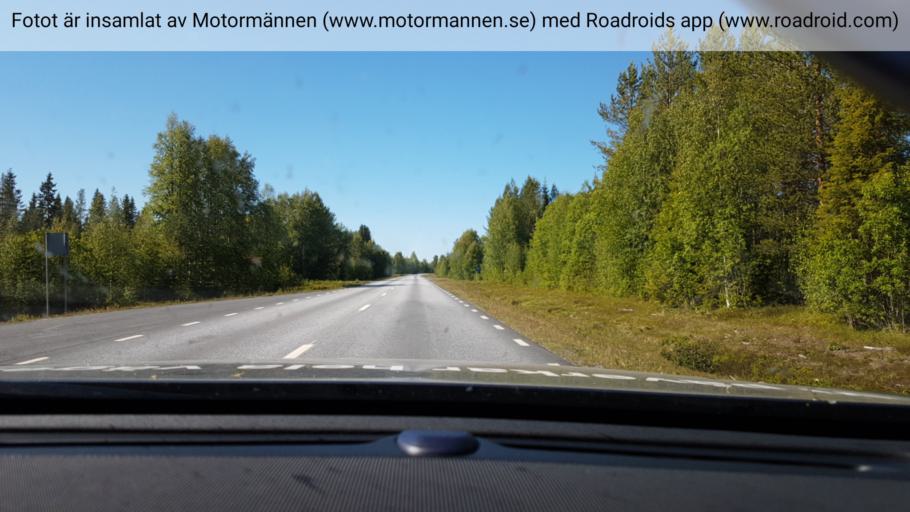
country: SE
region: Vaesterbotten
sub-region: Vilhelmina Kommun
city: Vilhelmina
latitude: 64.4599
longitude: 16.8089
